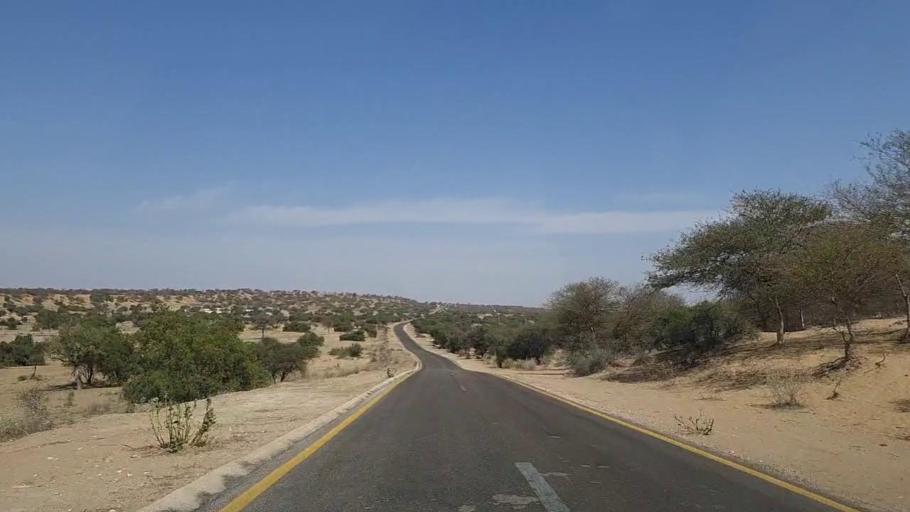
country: PK
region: Sindh
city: Mithi
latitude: 24.8866
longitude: 69.8747
